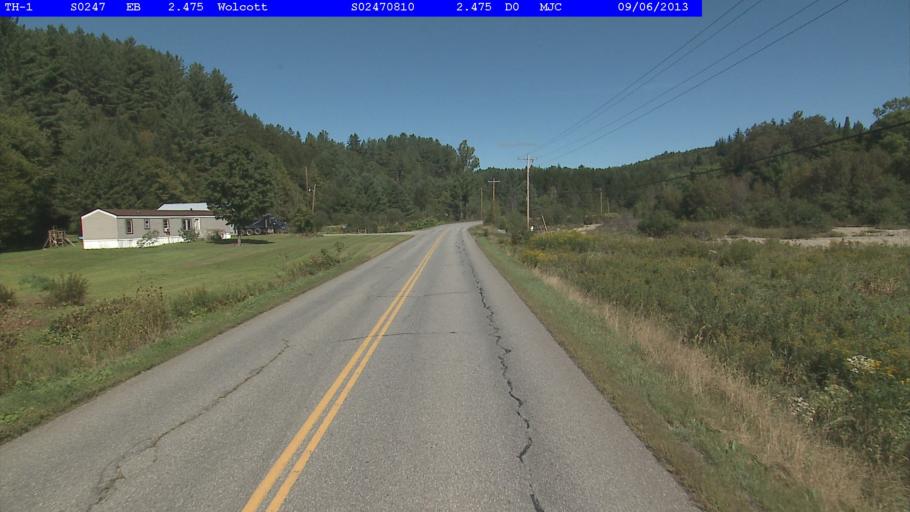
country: US
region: Vermont
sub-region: Lamoille County
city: Morrisville
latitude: 44.5911
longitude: -72.4740
